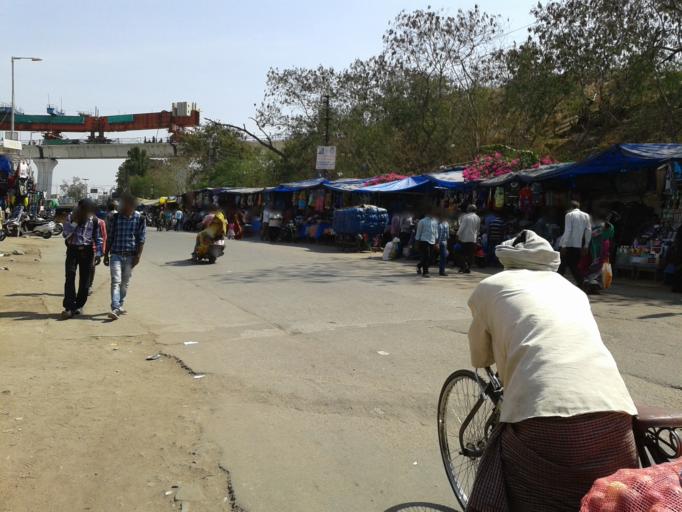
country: IN
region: Telangana
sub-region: Hyderabad
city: Malkajgiri
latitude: 17.4348
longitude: 78.4992
